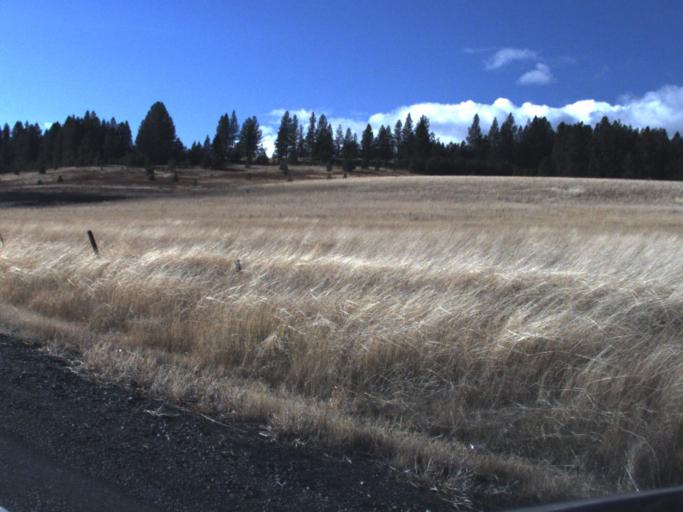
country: US
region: Washington
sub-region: Asotin County
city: Asotin
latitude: 46.1121
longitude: -117.1379
